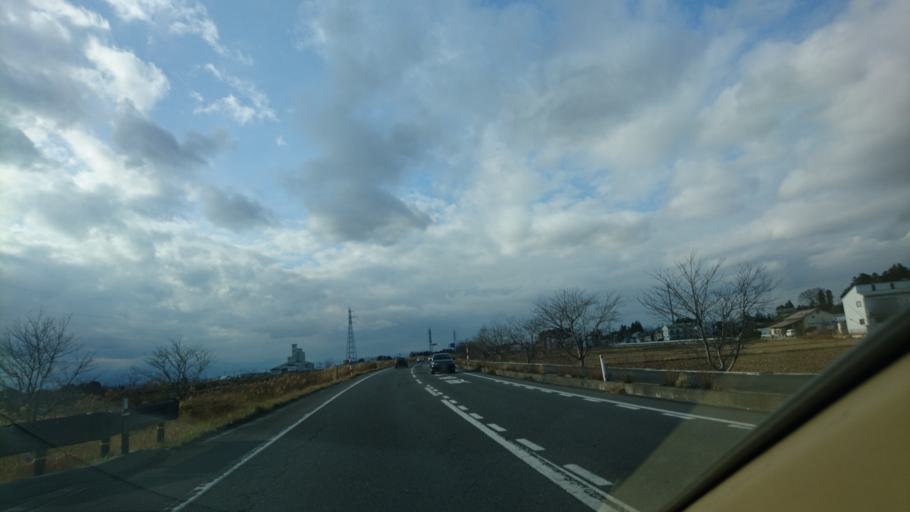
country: JP
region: Miyagi
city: Kogota
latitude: 38.5525
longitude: 141.0536
